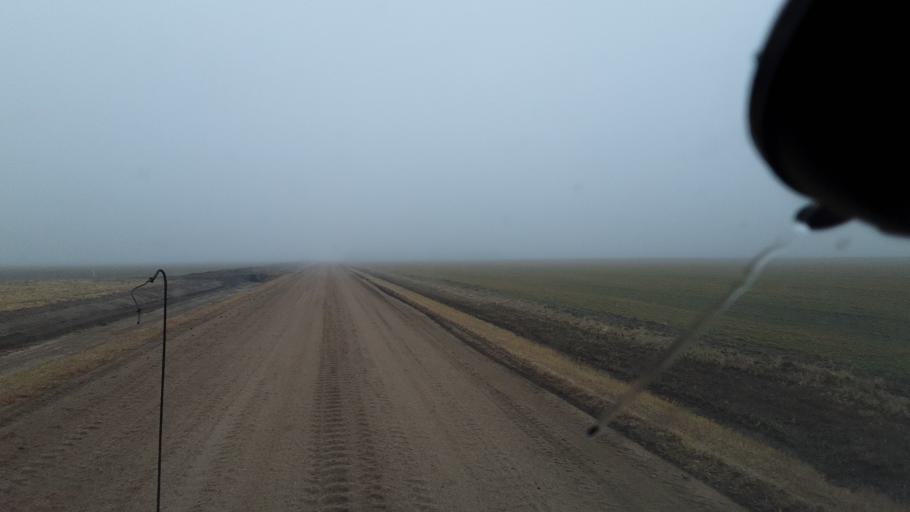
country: US
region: Kansas
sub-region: Reno County
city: South Hutchinson
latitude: 37.9842
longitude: -97.9804
